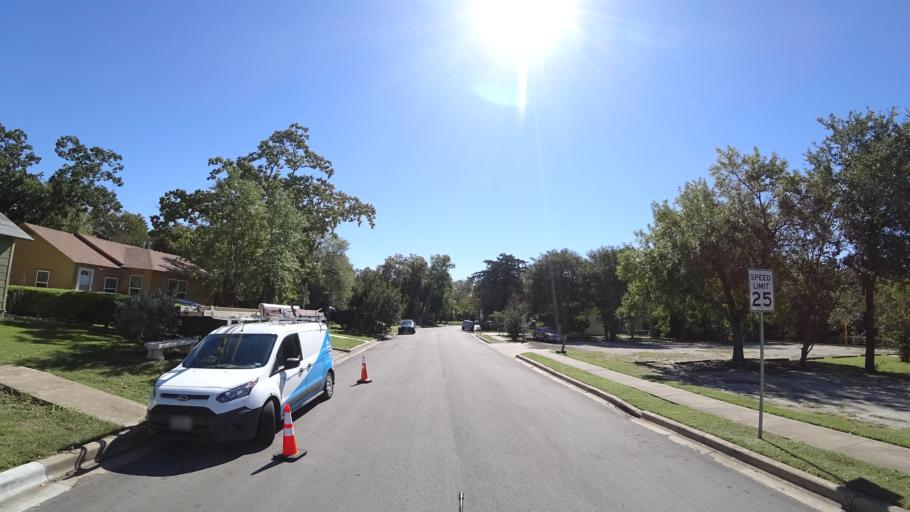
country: US
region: Texas
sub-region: Travis County
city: Austin
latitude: 30.2895
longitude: -97.7097
